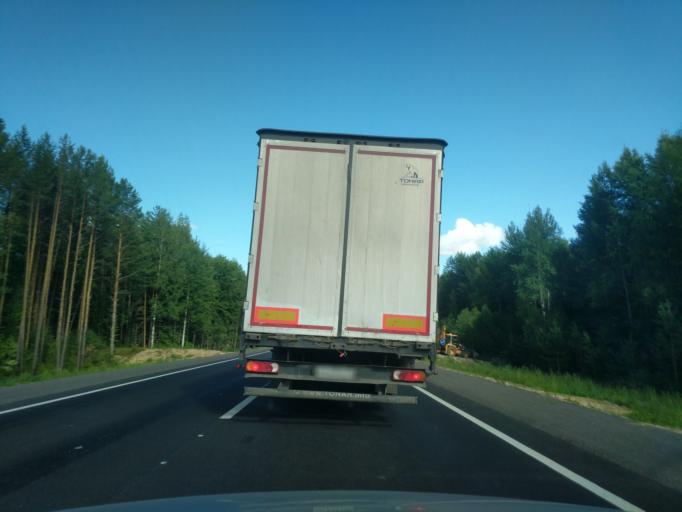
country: RU
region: Kostroma
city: Makar'yev
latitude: 57.8482
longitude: 43.6742
